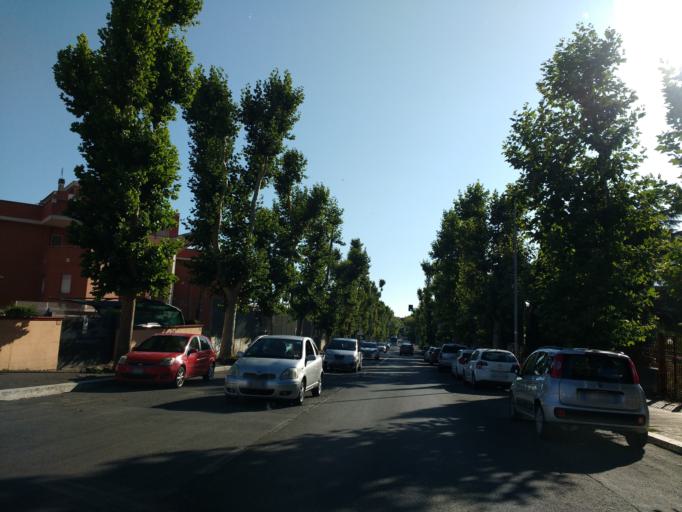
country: IT
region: Latium
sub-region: Citta metropolitana di Roma Capitale
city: Acilia-Castel Fusano-Ostia Antica
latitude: 41.7796
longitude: 12.3602
